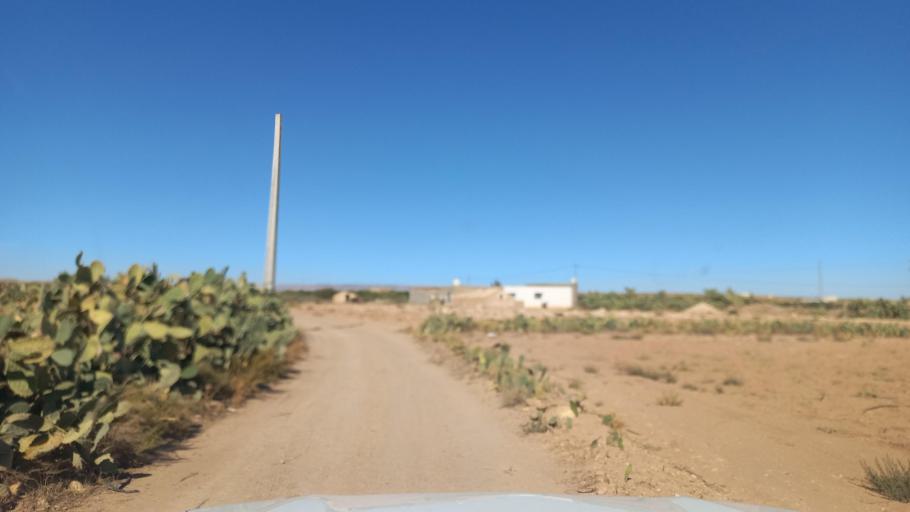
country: TN
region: Al Qasrayn
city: Sbiba
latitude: 35.3940
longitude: 9.0836
